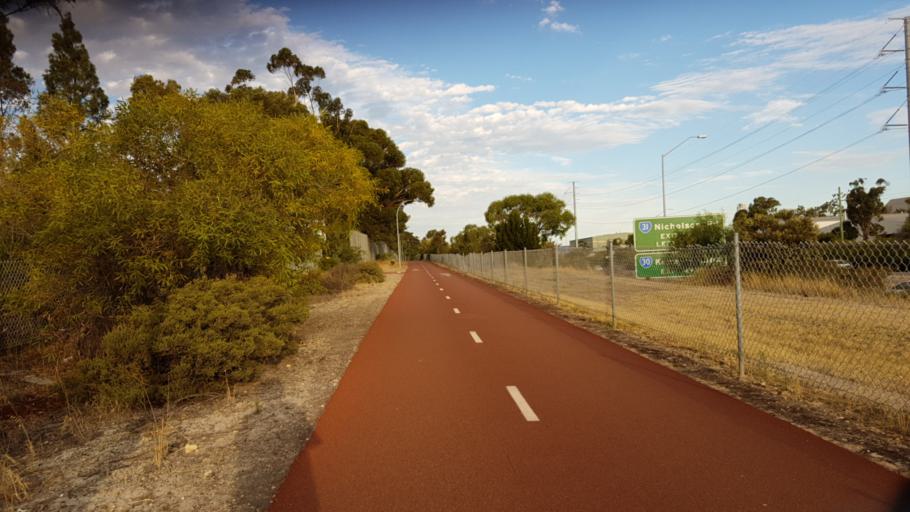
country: AU
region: Western Australia
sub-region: Canning
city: Canning Vale
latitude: -32.0542
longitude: 115.9136
